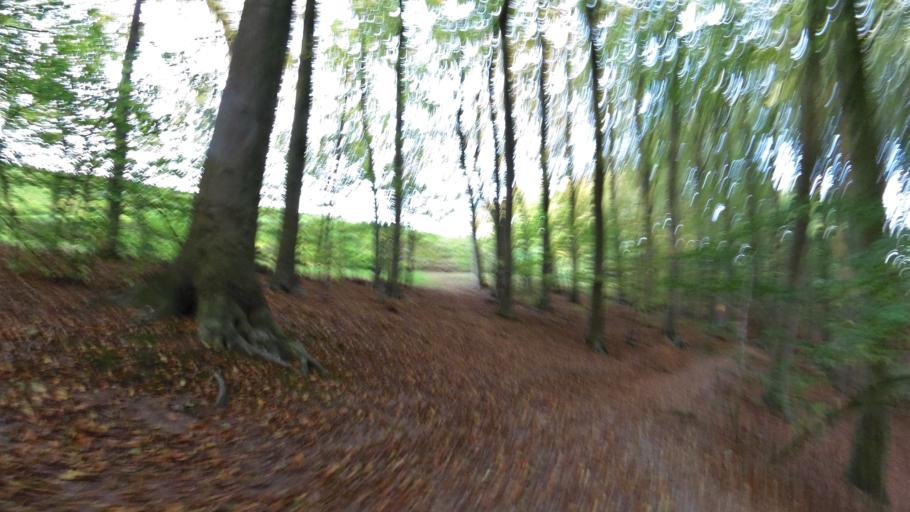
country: DK
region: Central Jutland
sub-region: Arhus Kommune
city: Stavtrup
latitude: 56.1579
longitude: 10.1152
